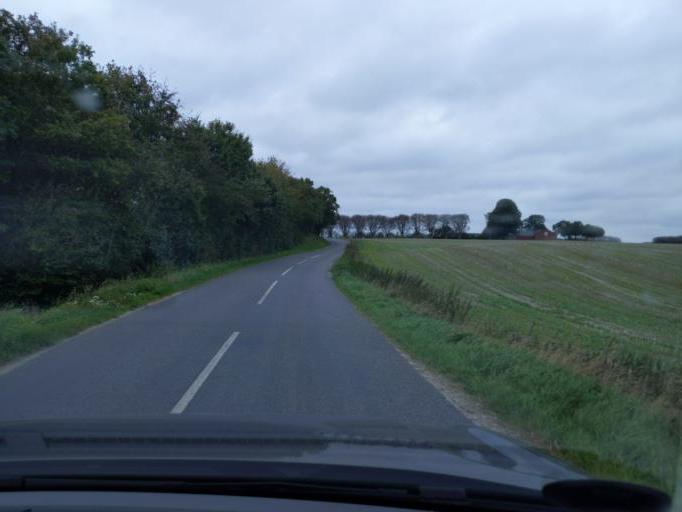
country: DK
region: Central Jutland
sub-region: Viborg Kommune
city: Bjerringbro
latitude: 56.5426
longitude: 9.6248
